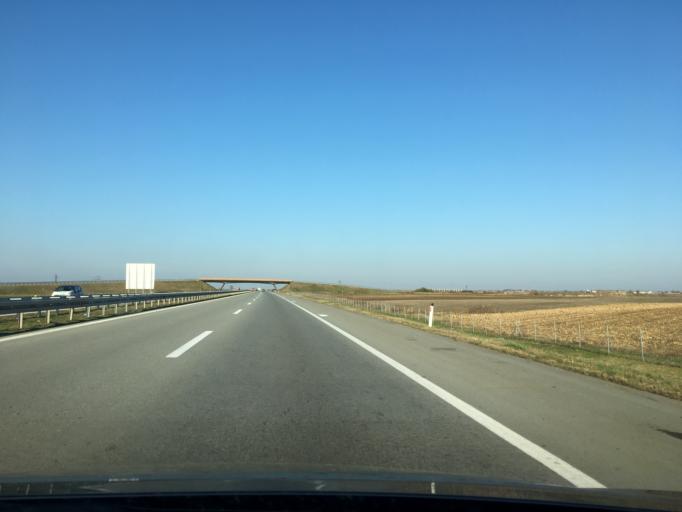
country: RS
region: Autonomna Pokrajina Vojvodina
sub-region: Juznobacki Okrug
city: Kovilj
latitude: 45.2497
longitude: 20.0218
